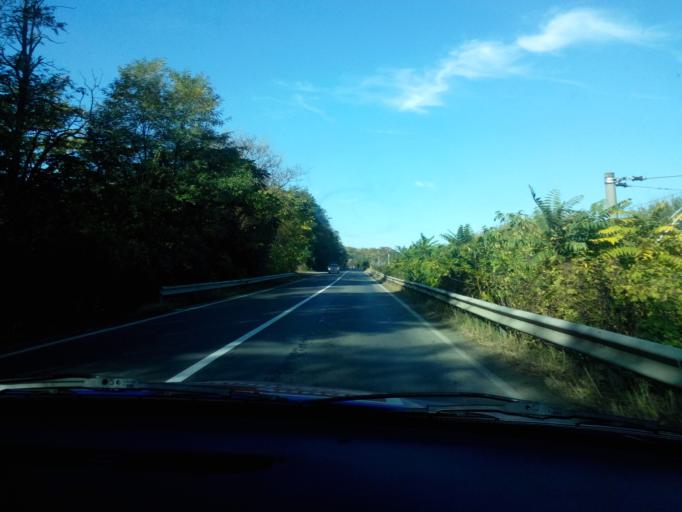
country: RO
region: Bacau
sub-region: Comuna Caiuti
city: Caiuti
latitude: 46.1910
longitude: 26.9047
